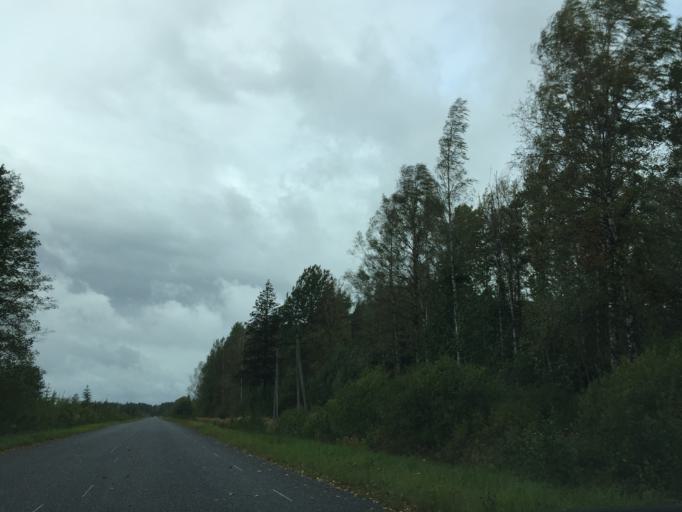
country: LV
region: Salacgrivas
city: Ainazi
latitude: 57.9706
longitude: 24.4350
